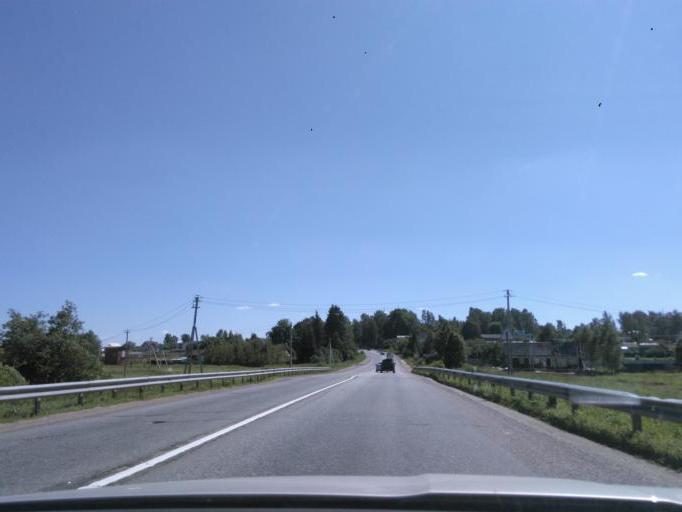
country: RU
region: Moskovskaya
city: Solnechnogorsk
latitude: 56.1527
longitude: 36.9193
